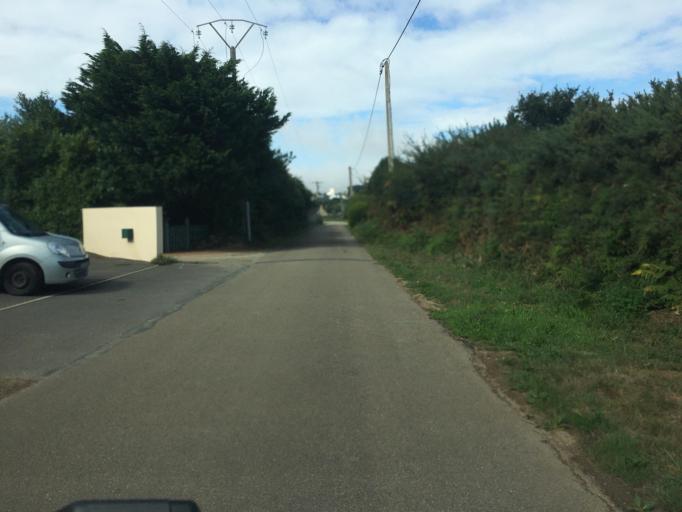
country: FR
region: Brittany
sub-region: Departement du Finistere
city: Beuzec-Cap-Sizun
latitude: 48.0751
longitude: -4.5002
